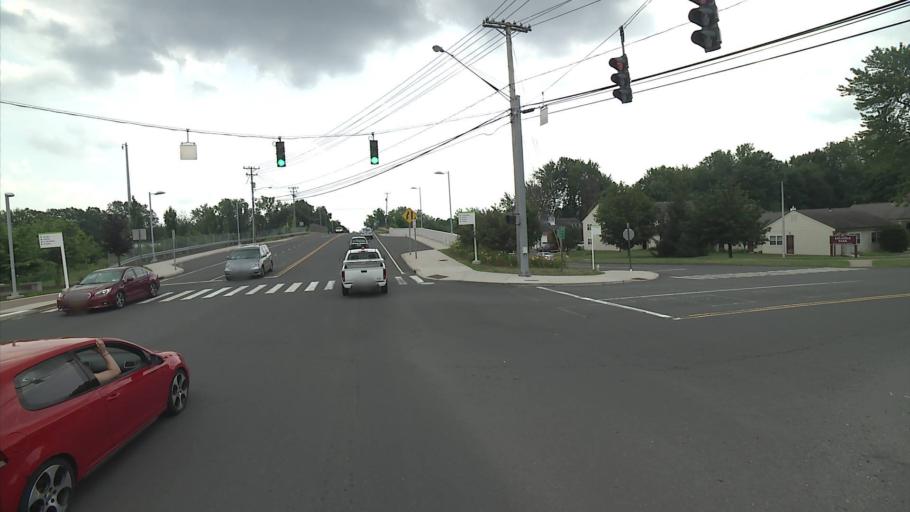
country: US
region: Connecticut
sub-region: Hartford County
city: Newington
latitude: 41.7165
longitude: -72.7374
